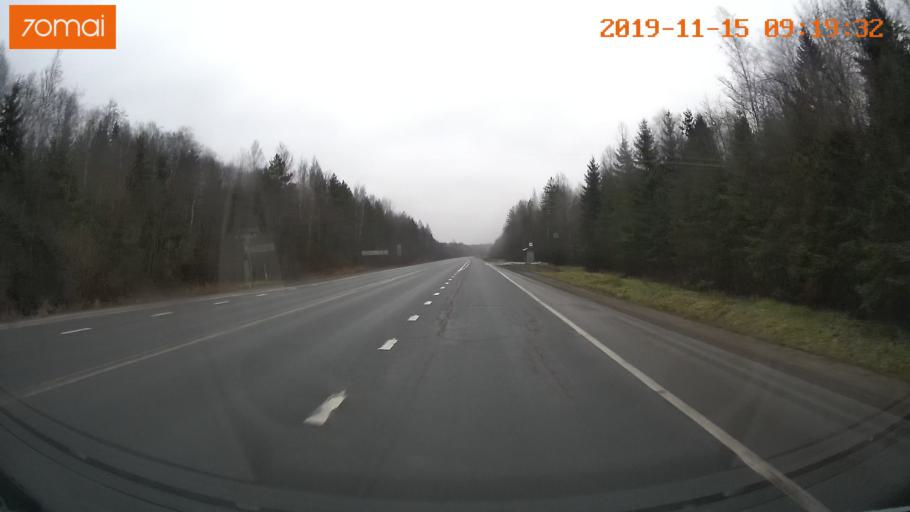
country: RU
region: Vologda
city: Tonshalovo
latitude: 59.2846
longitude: 38.0179
